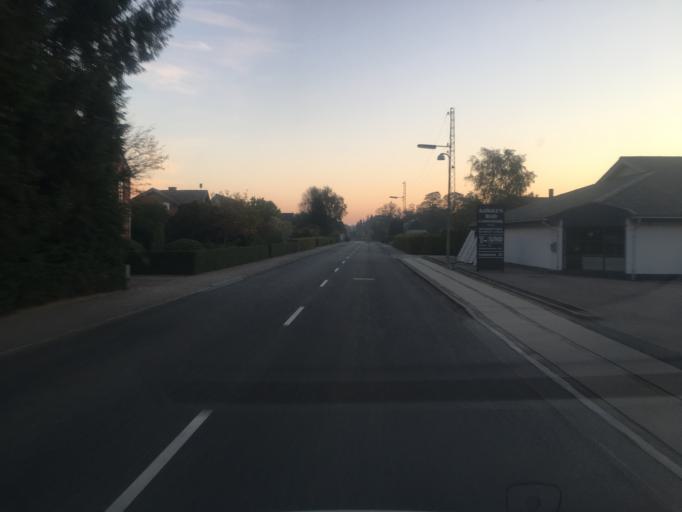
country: DE
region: Schleswig-Holstein
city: Bramstedtlund
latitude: 54.9501
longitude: 9.1007
